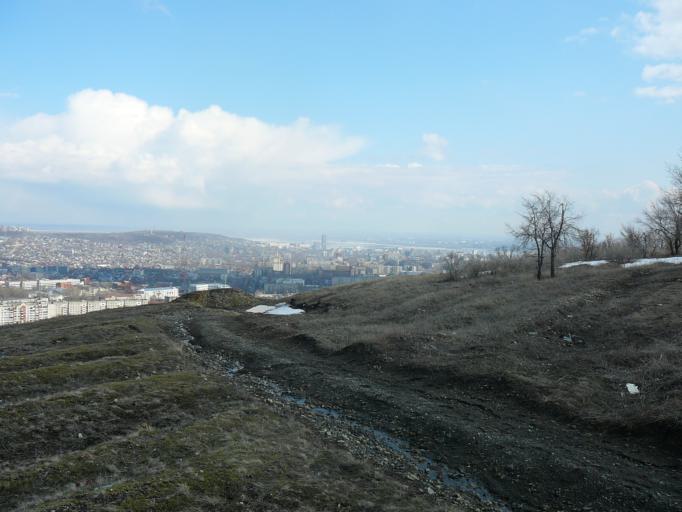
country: RU
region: Saratov
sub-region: Saratovskiy Rayon
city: Saratov
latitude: 51.5523
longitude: 45.9870
